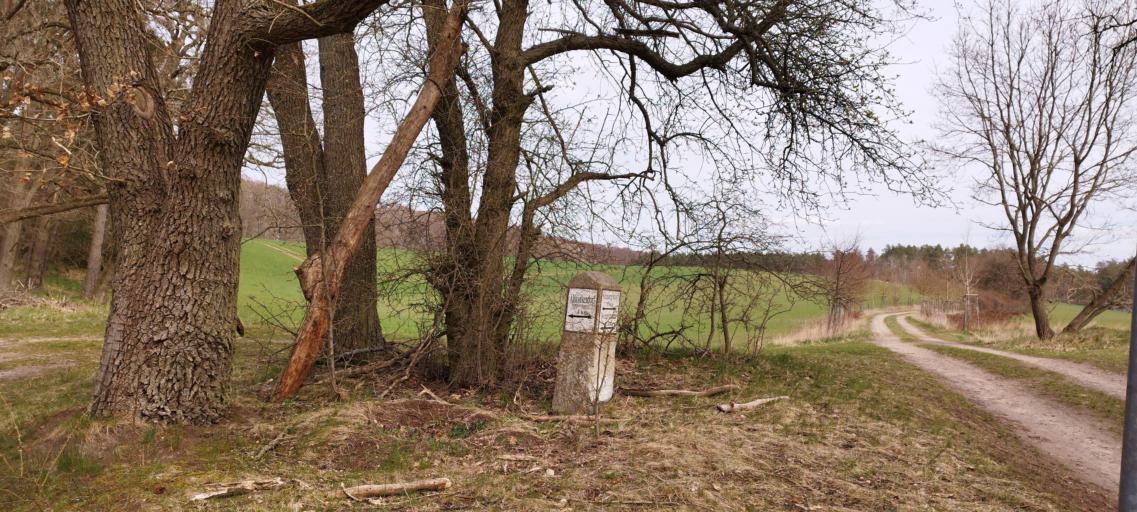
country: DE
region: Brandenburg
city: Althuttendorf
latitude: 52.9727
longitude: 13.8729
